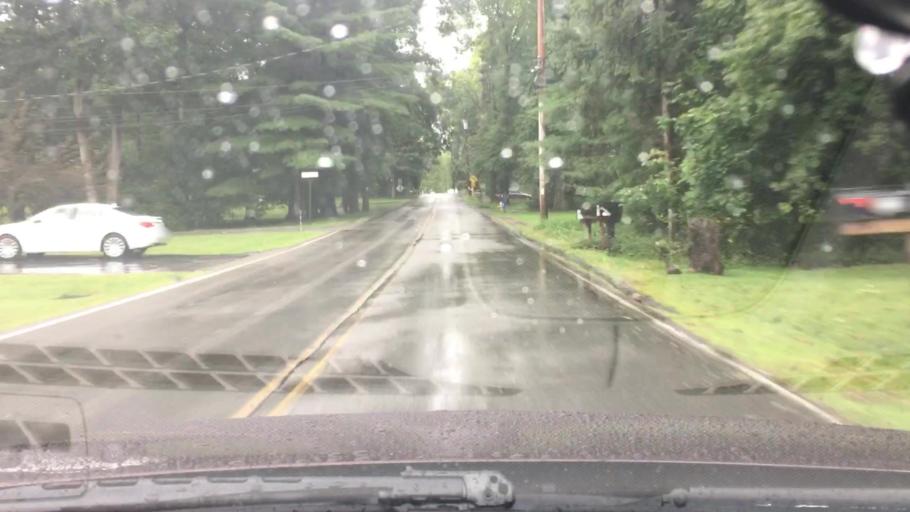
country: US
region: New York
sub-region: Dutchess County
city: Myers Corner
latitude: 41.5919
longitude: -73.8823
